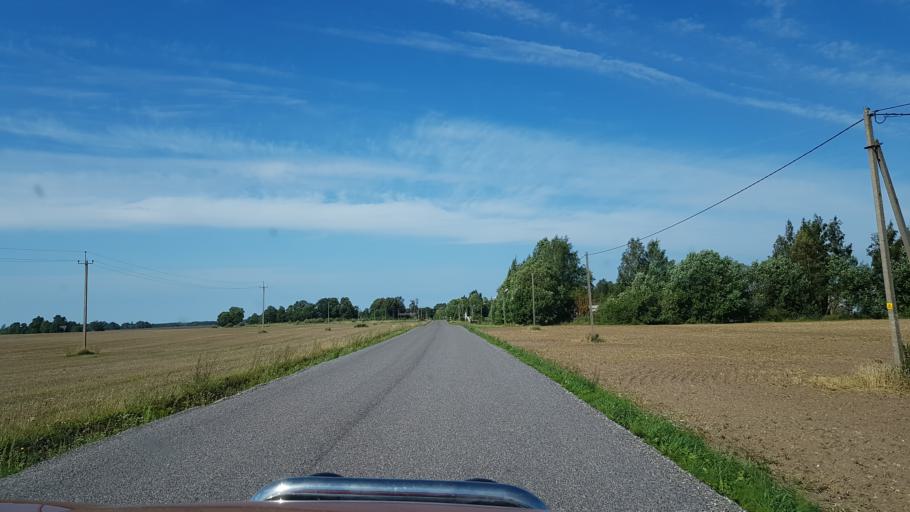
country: EE
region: Tartu
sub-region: Puhja vald
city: Puhja
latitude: 58.2592
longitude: 26.3102
